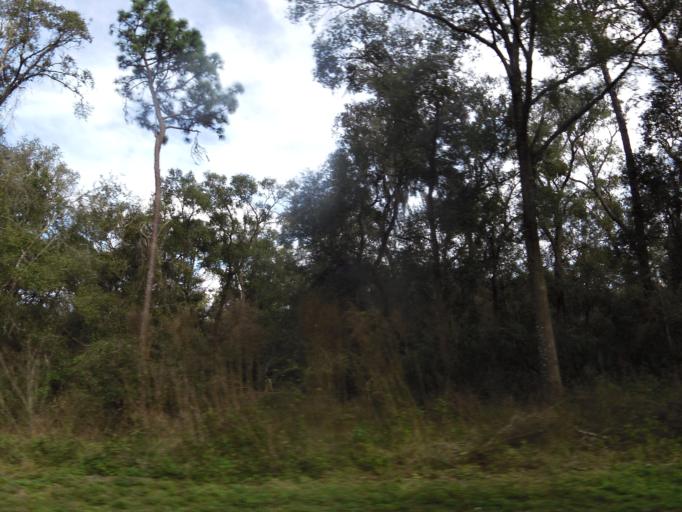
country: US
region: Florida
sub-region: Volusia County
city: Orange City
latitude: 28.9515
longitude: -81.2657
